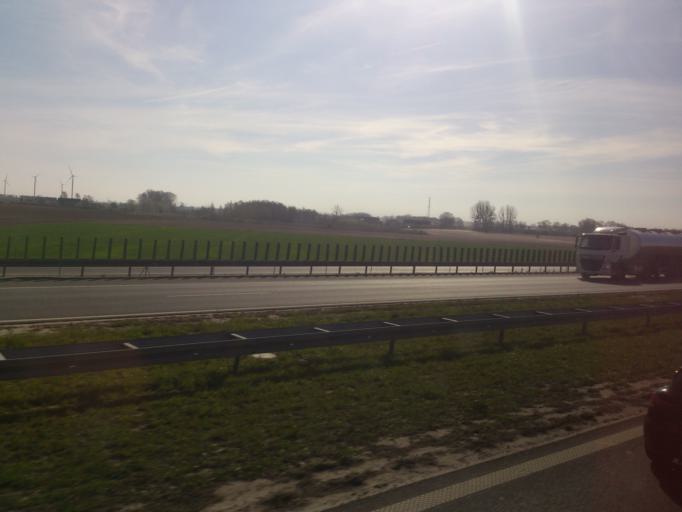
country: PL
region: Kujawsko-Pomorskie
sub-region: Powiat aleksandrowski
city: Raciazek
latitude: 52.8170
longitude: 18.8081
